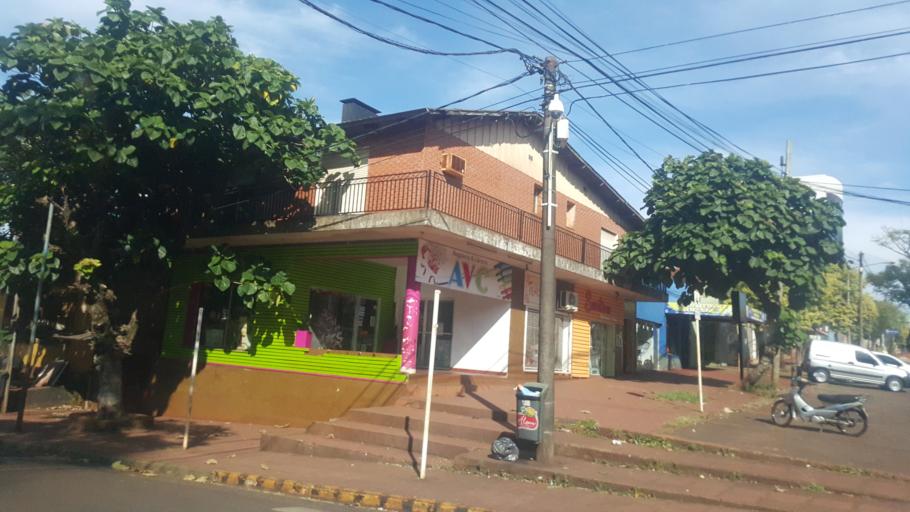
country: AR
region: Misiones
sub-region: Departamento de Leandro N. Alem
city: Leandro N. Alem
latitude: -27.6044
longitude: -55.3236
